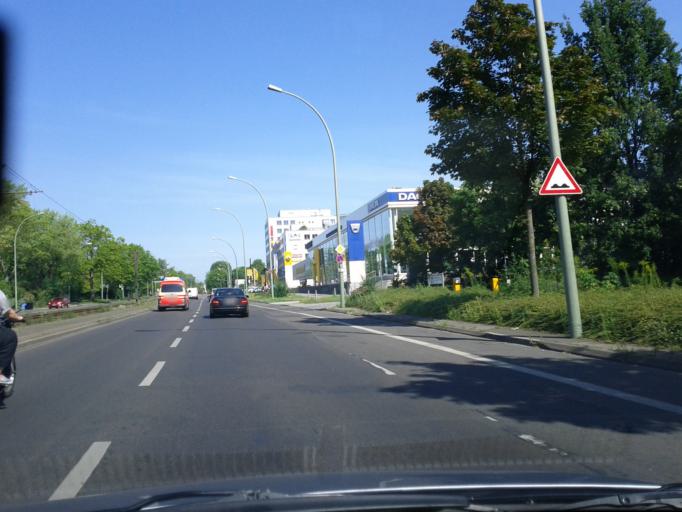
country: DE
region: Berlin
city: Fennpfuhl
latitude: 52.5335
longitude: 13.4760
